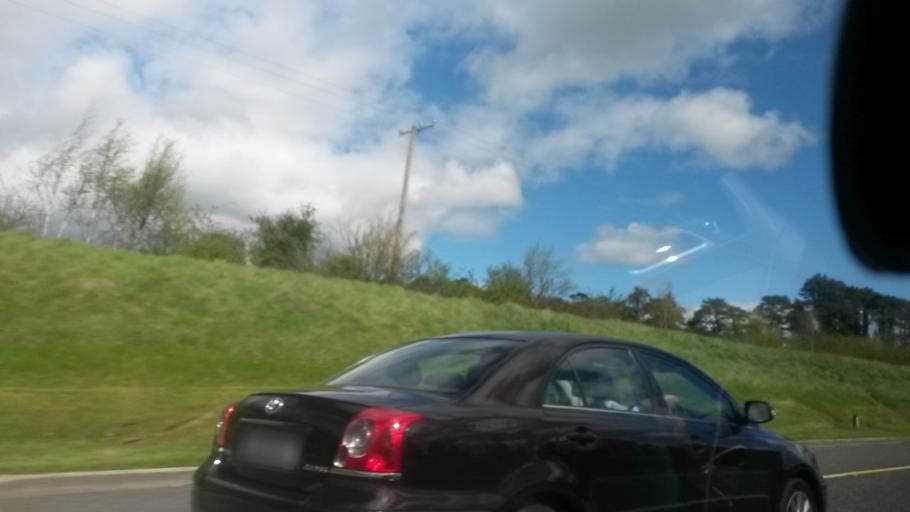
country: IE
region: Leinster
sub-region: Kildare
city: Kildare
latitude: 53.1513
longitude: -6.9022
